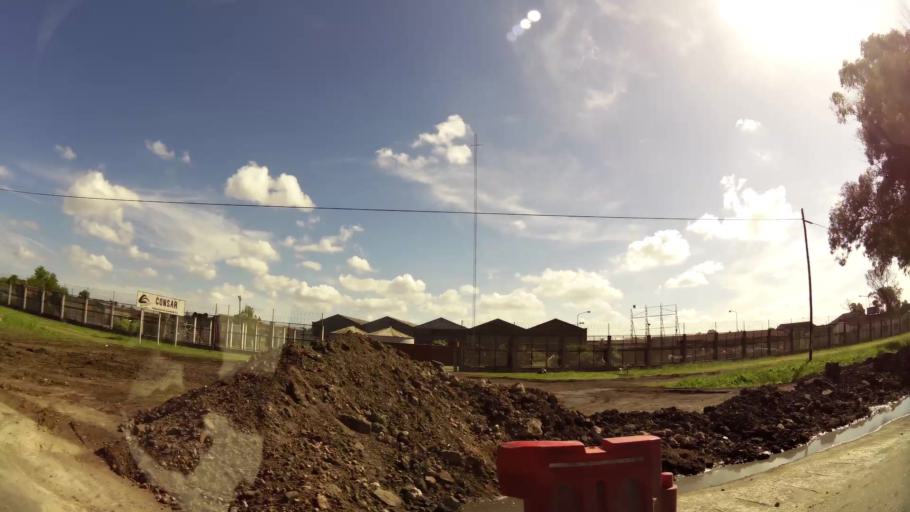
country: AR
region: Buenos Aires
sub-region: Partido de Quilmes
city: Quilmes
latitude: -34.7958
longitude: -58.2450
